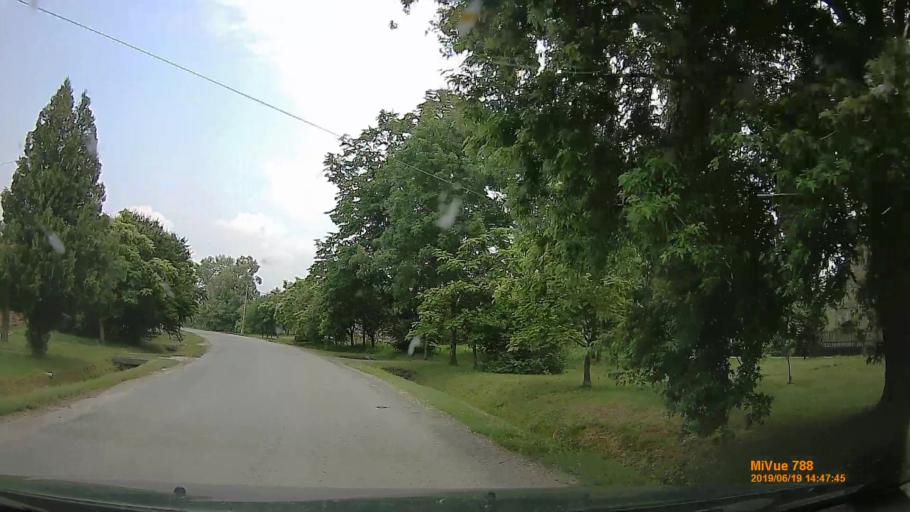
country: HU
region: Baranya
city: Szigetvar
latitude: 45.9952
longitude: 17.8319
